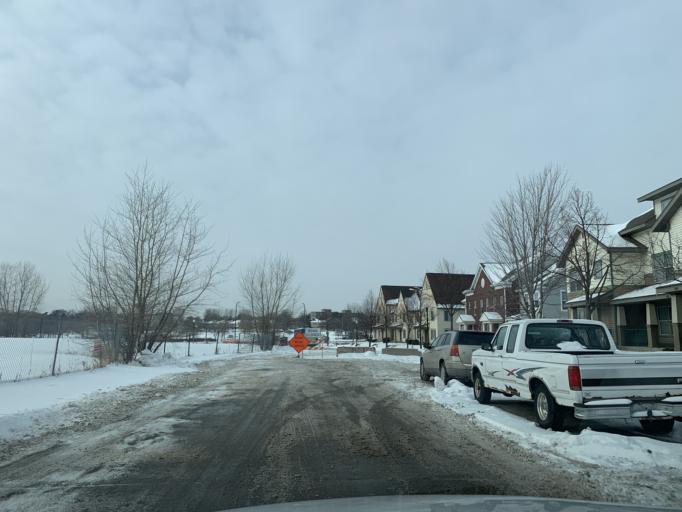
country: US
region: Minnesota
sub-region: Hennepin County
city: Minneapolis
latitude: 44.9828
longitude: -93.2915
